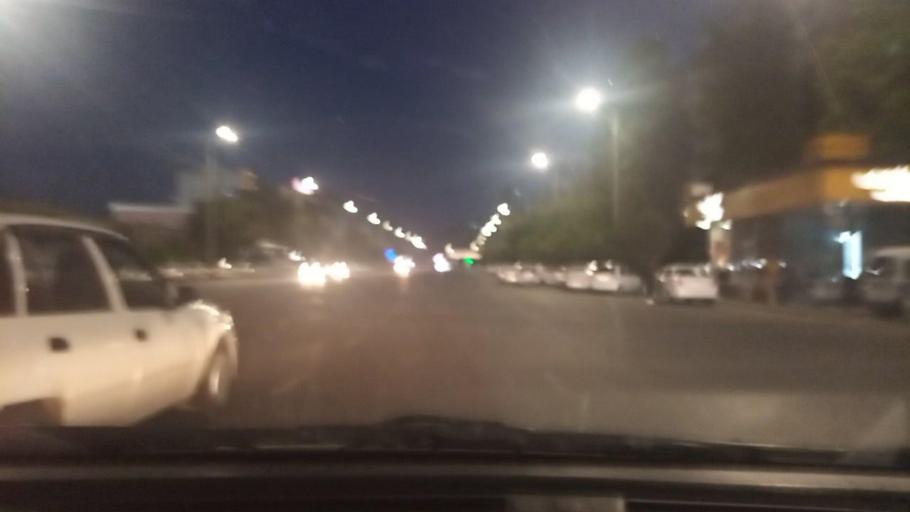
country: UZ
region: Toshkent Shahri
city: Tashkent
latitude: 41.2661
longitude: 69.2460
